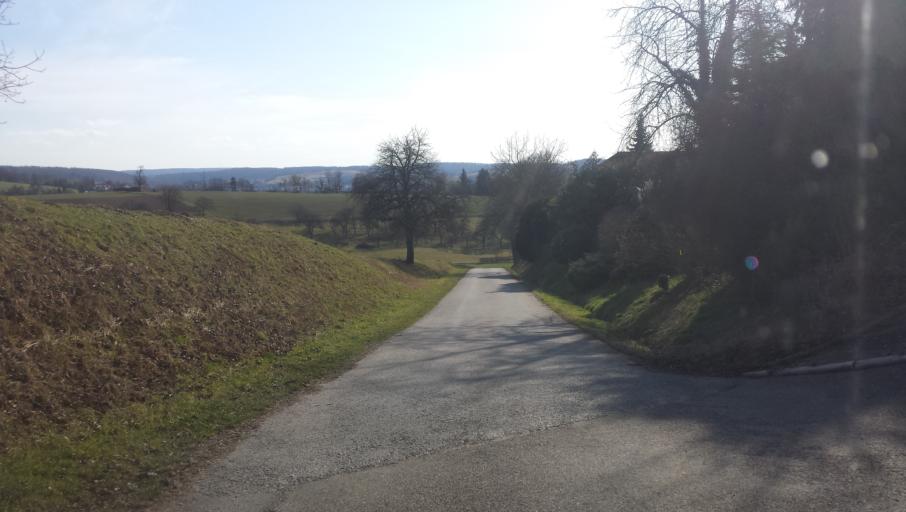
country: DE
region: Baden-Wuerttemberg
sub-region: Karlsruhe Region
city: Meckesheim
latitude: 49.3279
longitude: 8.8225
